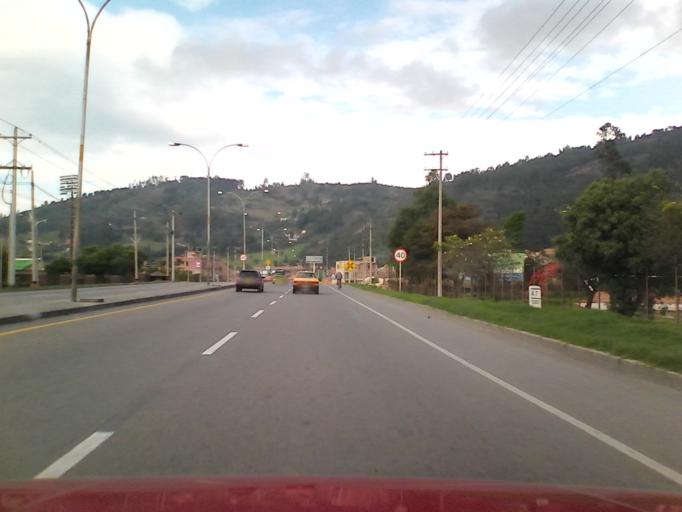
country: CO
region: Boyaca
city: Duitama
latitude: 5.8055
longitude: -73.0354
